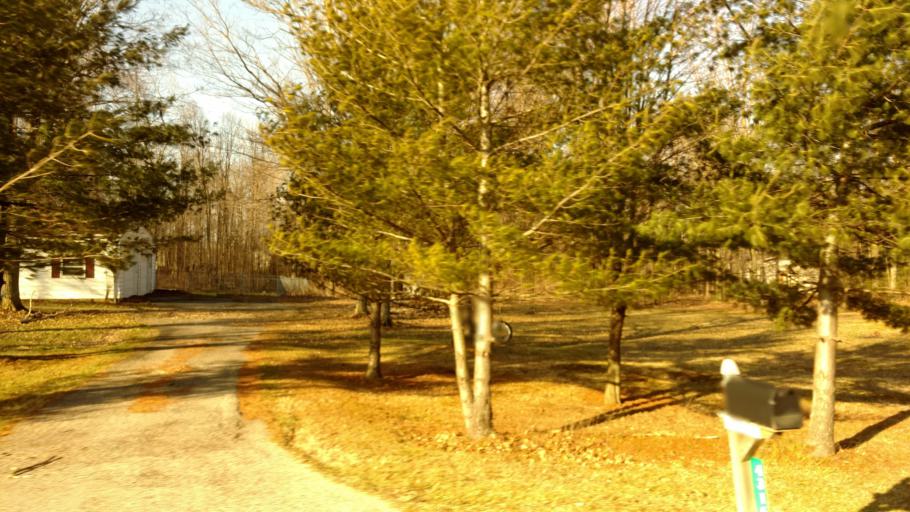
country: US
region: Ohio
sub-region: Richland County
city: Ontario
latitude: 40.7174
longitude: -82.6696
